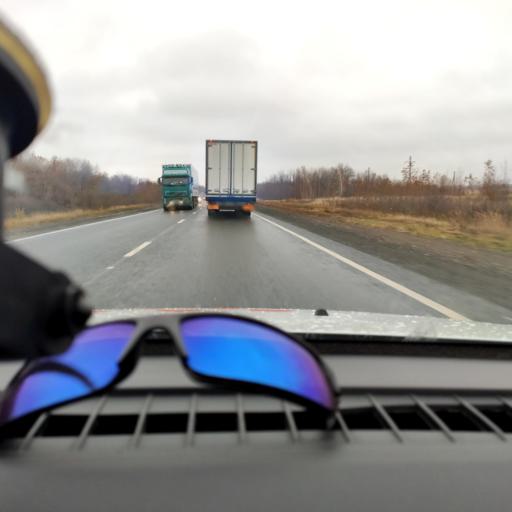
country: RU
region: Samara
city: Novokuybyshevsk
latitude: 52.9885
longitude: 49.9294
